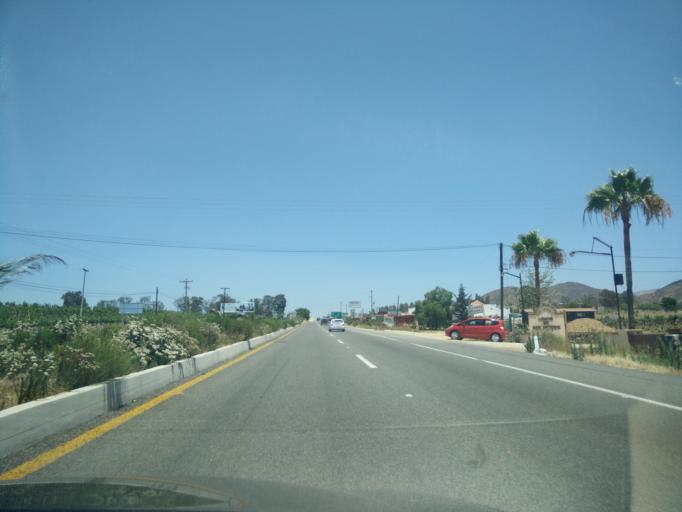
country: MX
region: Baja California
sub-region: Ensenada
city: Rancho Verde
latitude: 31.9894
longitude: -116.6434
